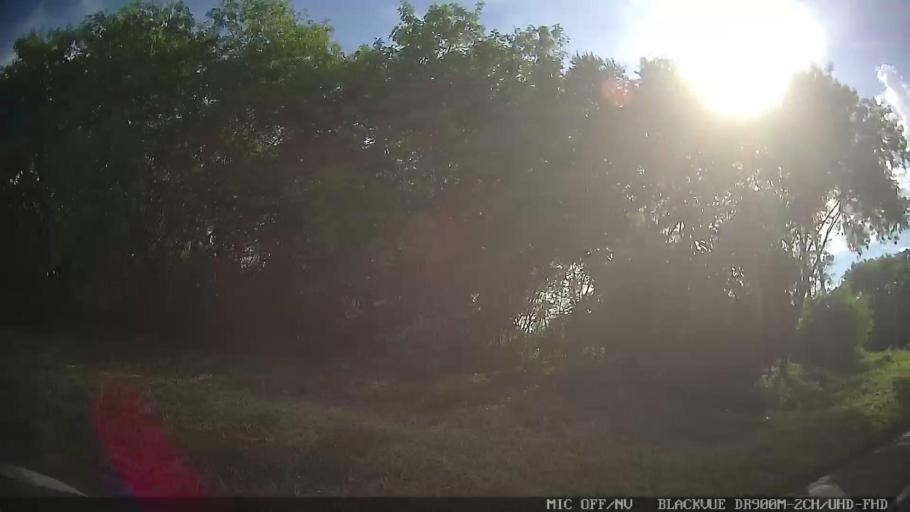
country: BR
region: Sao Paulo
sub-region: Laranjal Paulista
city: Laranjal Paulista
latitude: -23.0659
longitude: -47.8191
